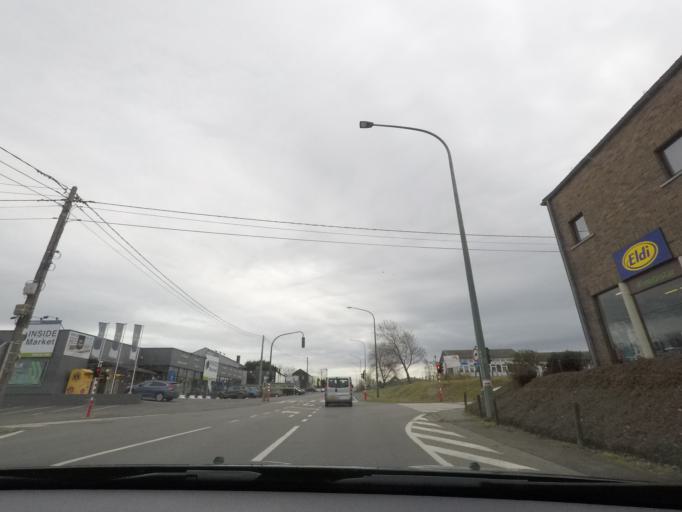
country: BE
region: Wallonia
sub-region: Province du Luxembourg
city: Bastogne
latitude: 49.9956
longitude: 5.7238
